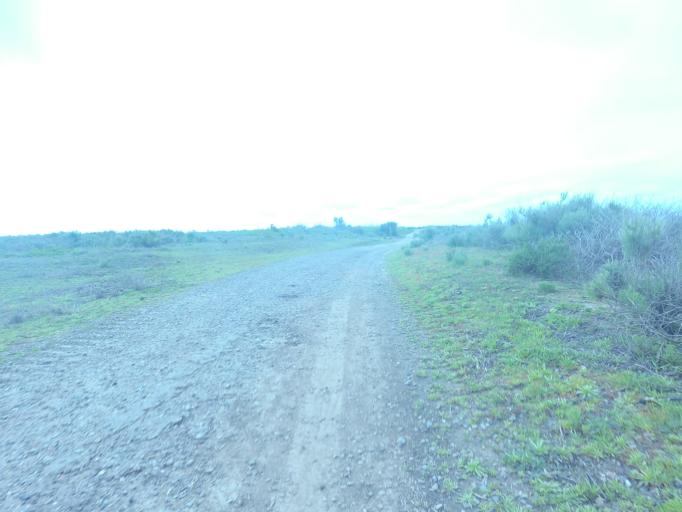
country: US
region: California
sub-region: Orange County
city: Laguna Beach
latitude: 33.5715
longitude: -117.7985
